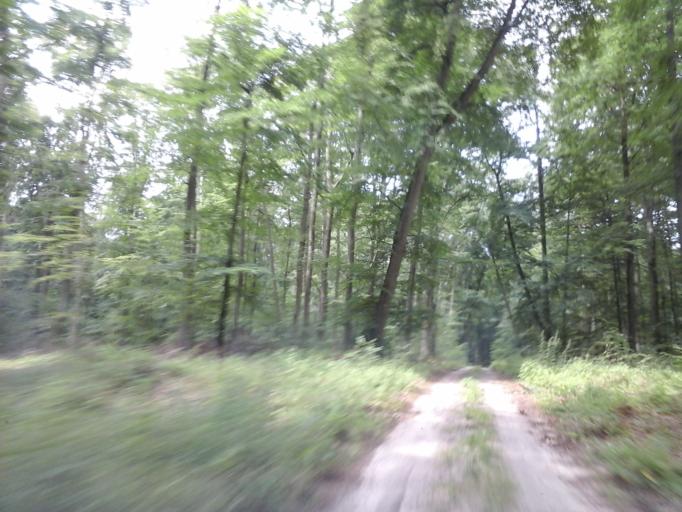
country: PL
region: West Pomeranian Voivodeship
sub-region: Powiat choszczenski
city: Bierzwnik
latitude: 53.0401
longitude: 15.5915
